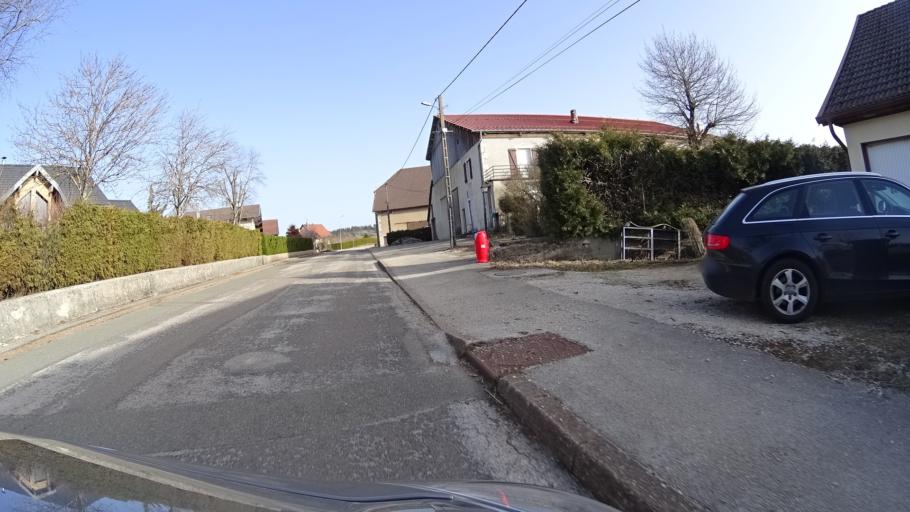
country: FR
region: Franche-Comte
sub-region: Departement du Doubs
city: Pontarlier
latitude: 46.8788
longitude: 6.2685
